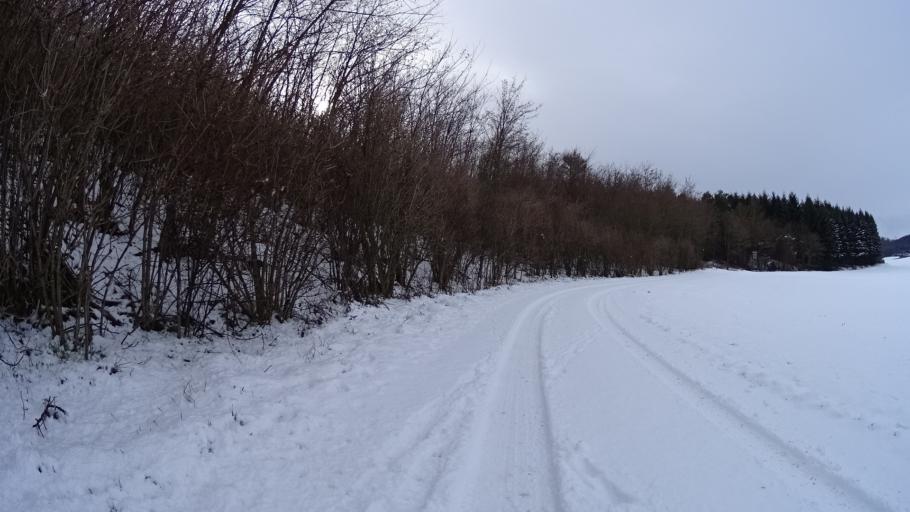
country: AT
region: Lower Austria
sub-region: Politischer Bezirk Korneuburg
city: Leobendorf
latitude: 48.3978
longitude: 16.3407
